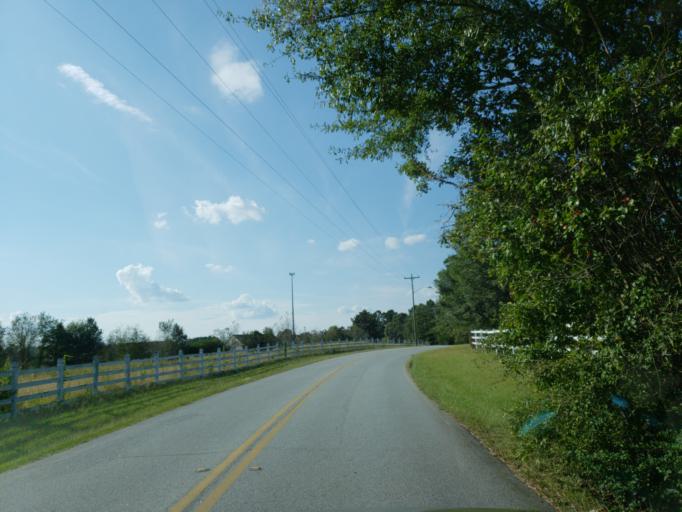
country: US
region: Georgia
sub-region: Paulding County
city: Hiram
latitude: 33.8780
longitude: -84.7232
